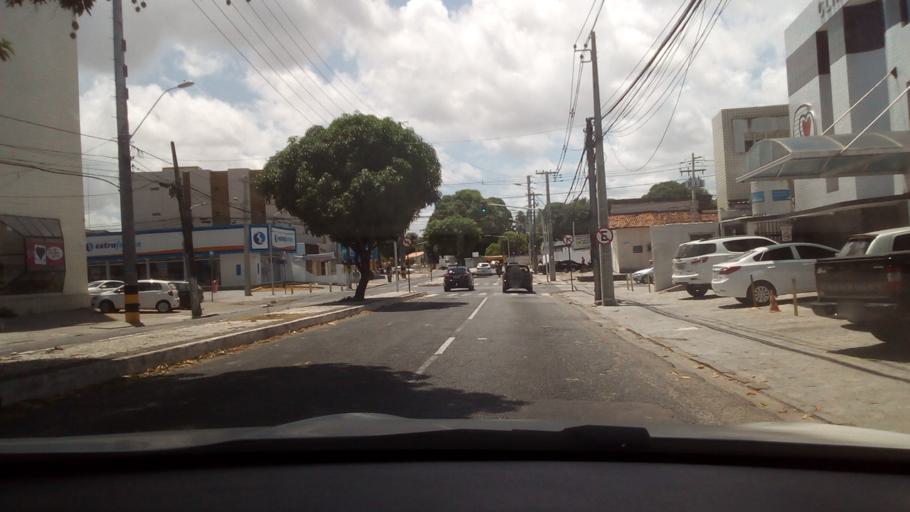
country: BR
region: Paraiba
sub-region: Joao Pessoa
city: Joao Pessoa
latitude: -7.1252
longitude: -34.8733
